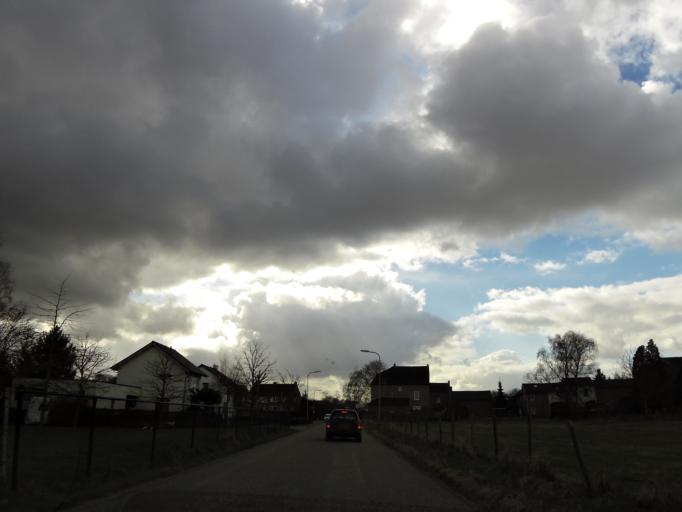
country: NL
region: Limburg
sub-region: Gemeente Onderbanken
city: Merkelbeek
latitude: 50.9742
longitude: 5.9326
